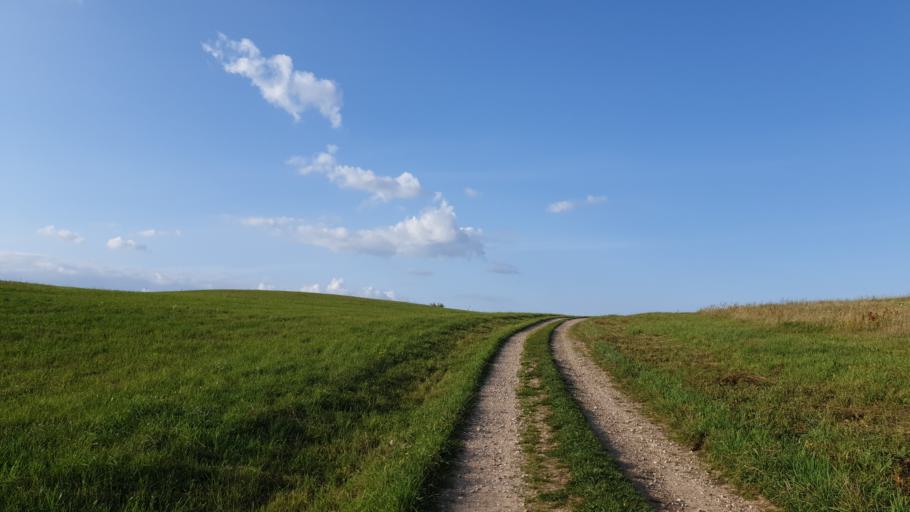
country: LT
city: Grigiskes
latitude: 54.7712
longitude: 25.0310
